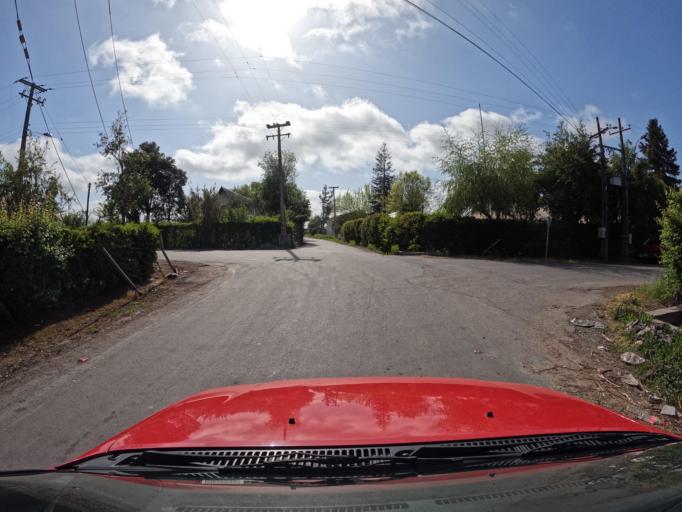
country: CL
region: Maule
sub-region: Provincia de Curico
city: Rauco
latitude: -34.8868
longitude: -71.2604
